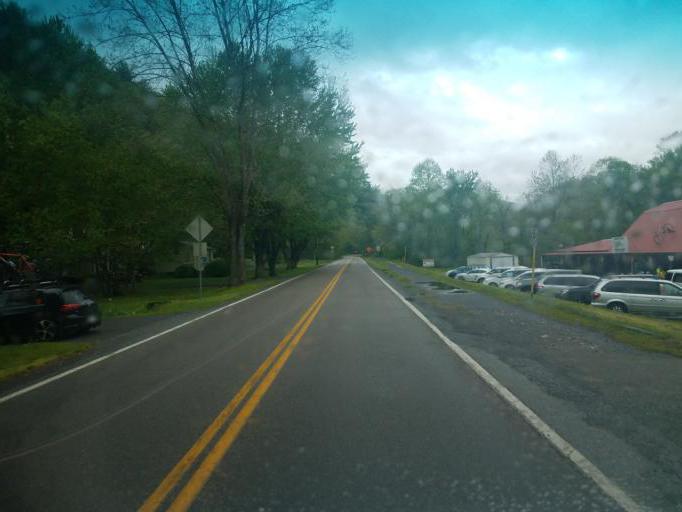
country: US
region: Virginia
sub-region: Washington County
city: Emory
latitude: 36.6304
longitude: -81.7824
